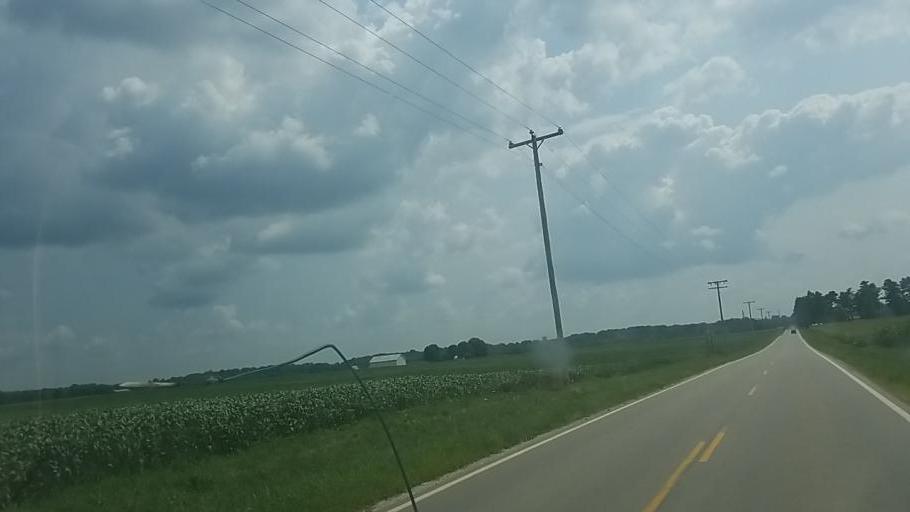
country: US
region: Ohio
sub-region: Wyandot County
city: Upper Sandusky
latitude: 40.8391
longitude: -83.1316
